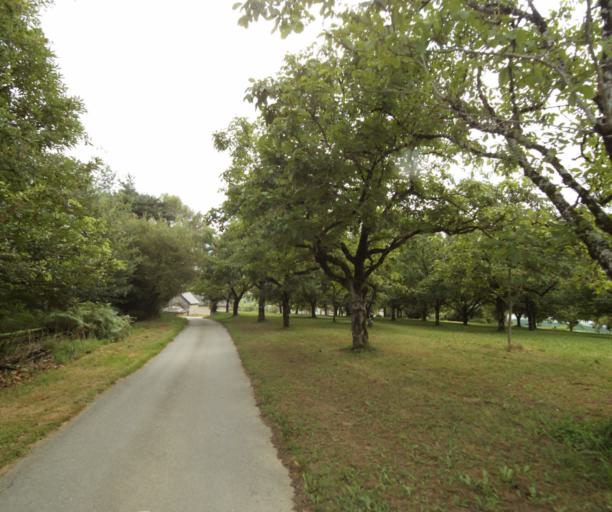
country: FR
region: Limousin
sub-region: Departement de la Correze
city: Sainte-Fortunade
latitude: 45.1709
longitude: 1.8385
